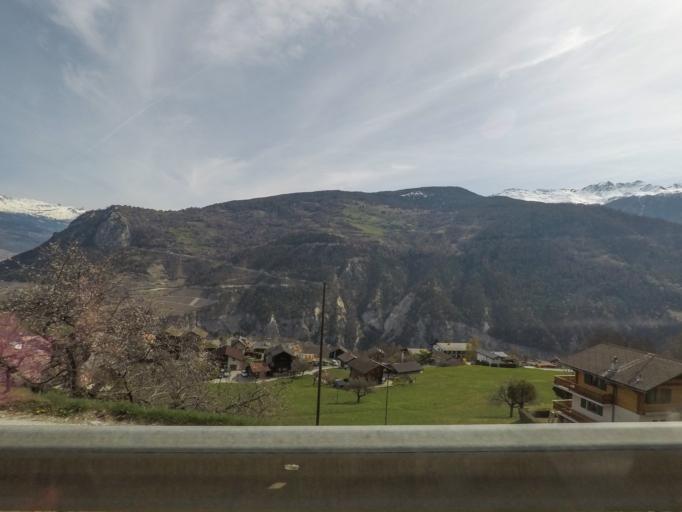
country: CH
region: Valais
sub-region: Herens District
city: Vex
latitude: 46.2075
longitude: 7.3985
